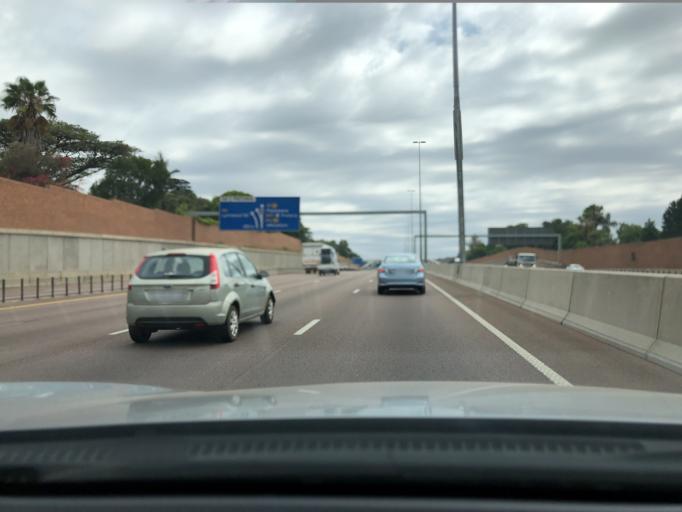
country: ZA
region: Gauteng
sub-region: City of Tshwane Metropolitan Municipality
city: Pretoria
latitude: -25.7736
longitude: 28.2730
